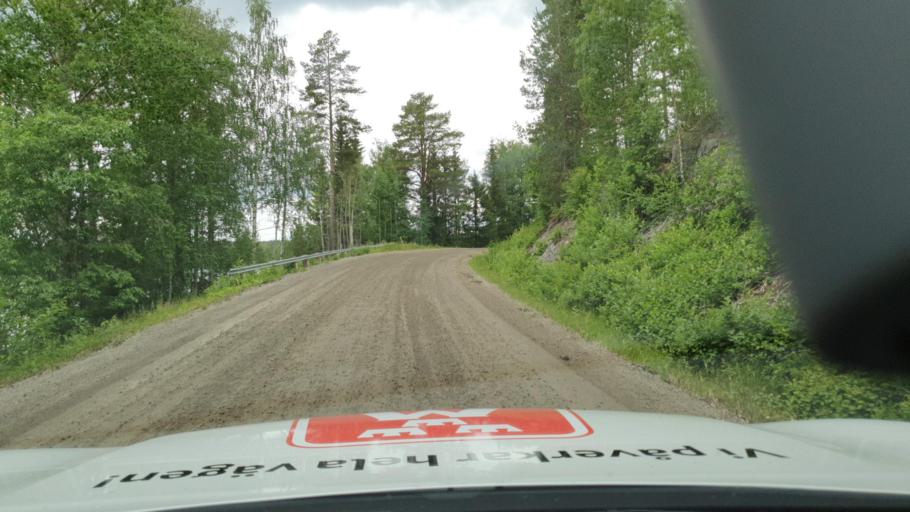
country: SE
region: Vaesterbotten
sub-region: Bjurholms Kommun
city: Bjurholm
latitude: 63.8348
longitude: 19.0012
